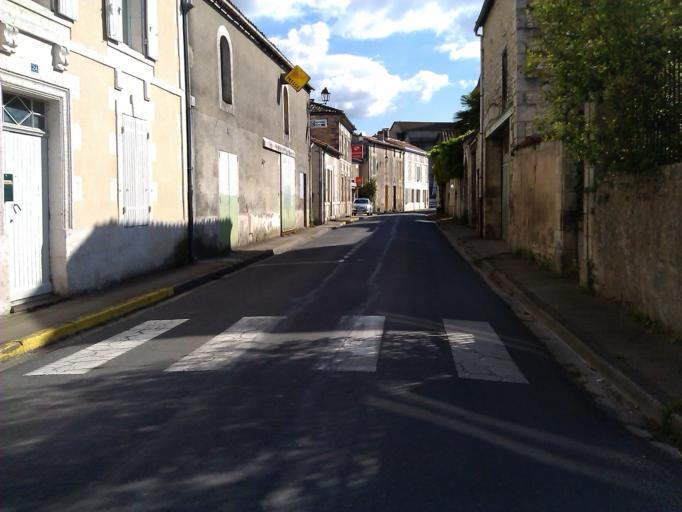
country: FR
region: Poitou-Charentes
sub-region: Departement de la Charente
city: Saint-Amant-de-Boixe
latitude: 45.7980
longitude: 0.1357
